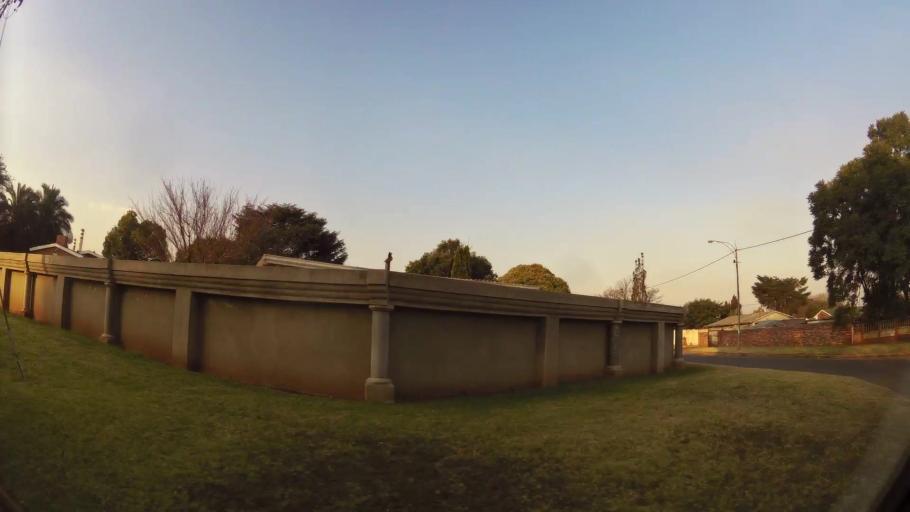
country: ZA
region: Gauteng
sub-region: Ekurhuleni Metropolitan Municipality
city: Springs
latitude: -26.2665
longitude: 28.4073
